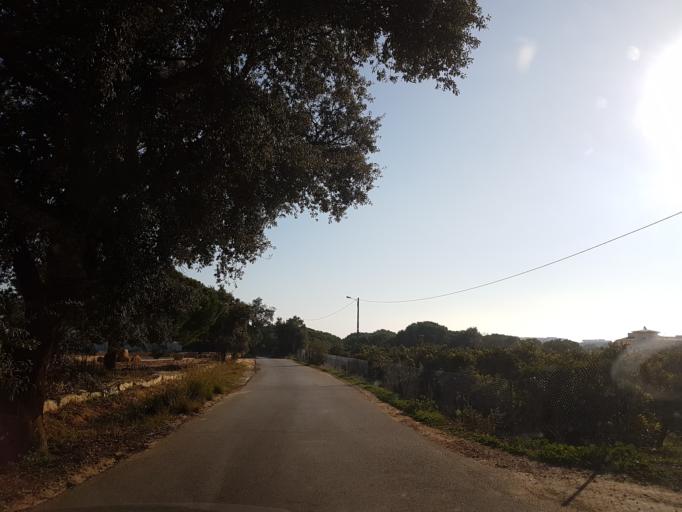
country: PT
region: Faro
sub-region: Albufeira
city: Ferreiras
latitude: 37.0990
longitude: -8.2050
